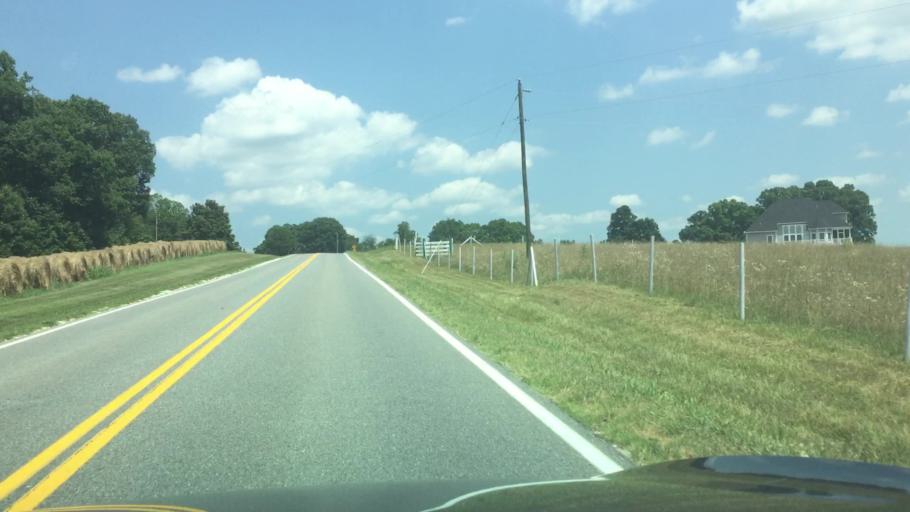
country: US
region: Virginia
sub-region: Appomattox County
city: Appomattox
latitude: 37.3394
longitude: -78.8817
